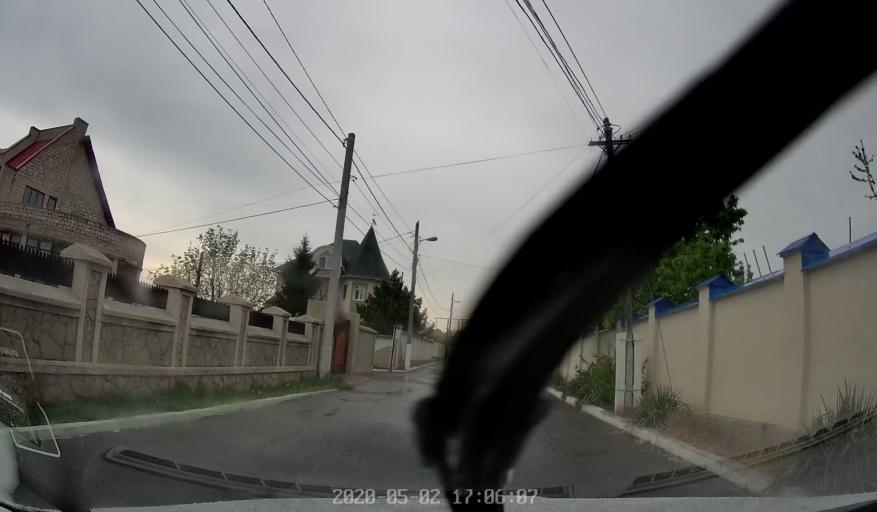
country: MD
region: Chisinau
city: Chisinau
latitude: 46.9691
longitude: 28.8327
